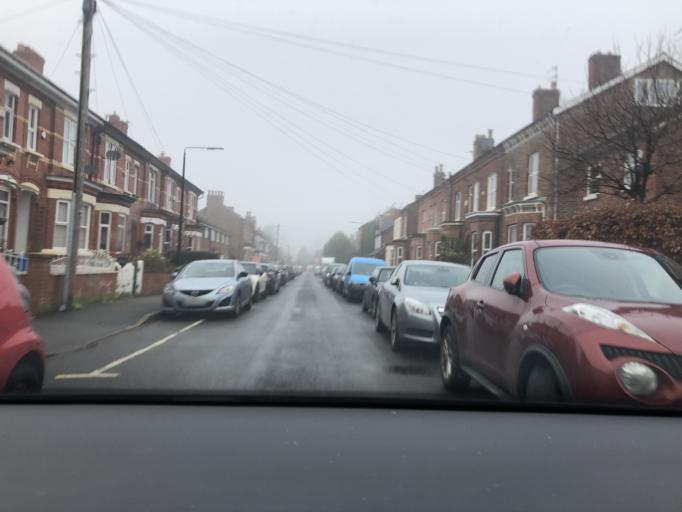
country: GB
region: England
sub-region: Trafford
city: Urmston
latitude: 53.4505
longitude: -2.3582
